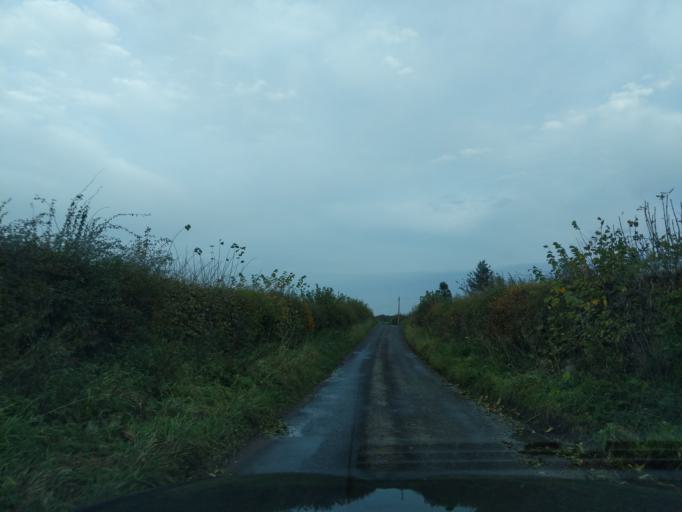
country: GB
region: Scotland
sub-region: Fife
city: Newport-On-Tay
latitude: 56.4218
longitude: -2.9158
